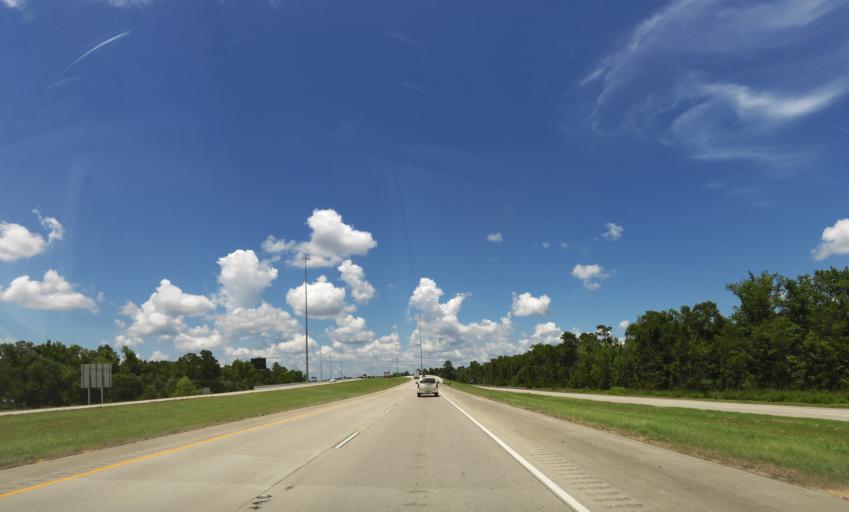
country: US
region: Texas
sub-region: San Jacinto County
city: Shepherd
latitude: 30.4954
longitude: -94.9904
